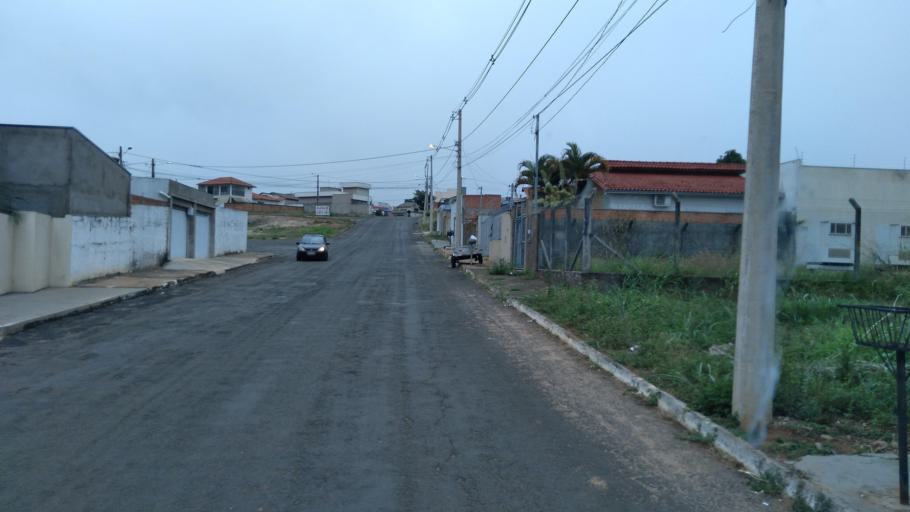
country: BR
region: Goias
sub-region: Mineiros
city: Mineiros
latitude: -17.5740
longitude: -52.5455
